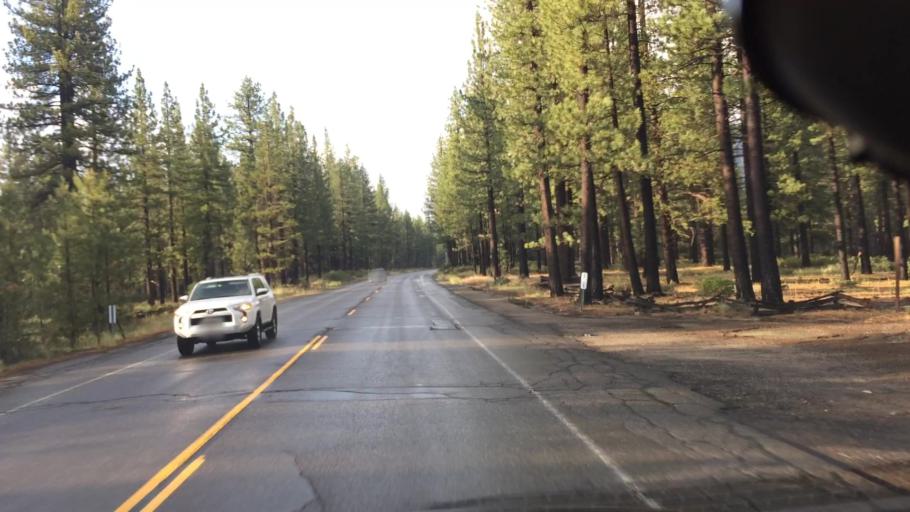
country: US
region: California
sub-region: El Dorado County
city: South Lake Tahoe
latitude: 38.8926
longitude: -119.9734
